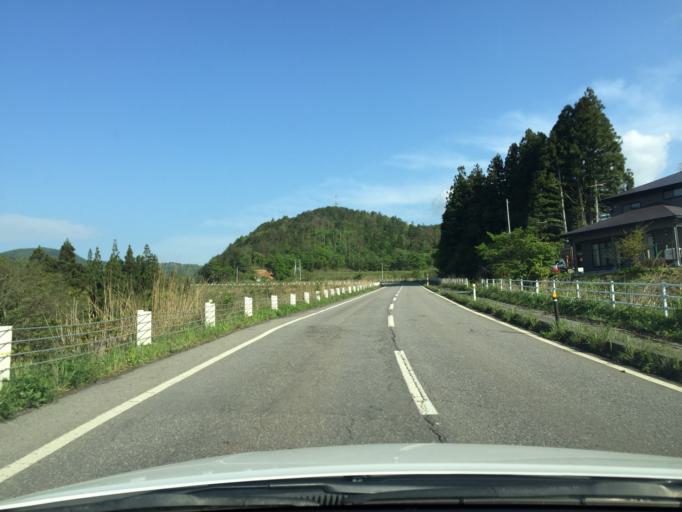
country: JP
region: Fukushima
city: Kitakata
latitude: 37.6494
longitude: 139.7715
